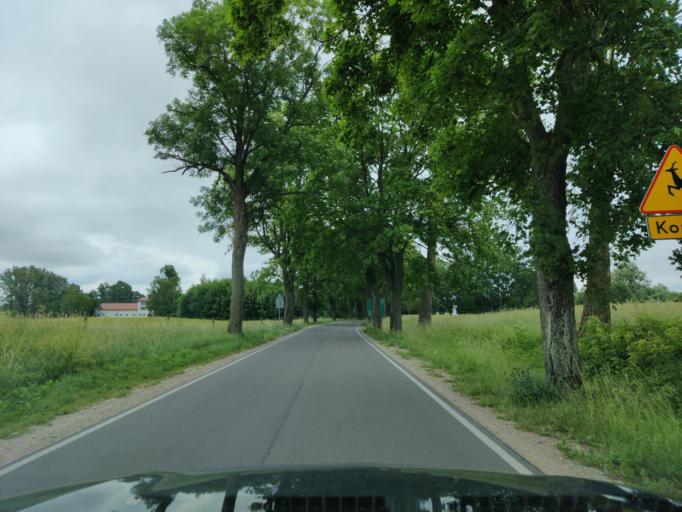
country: PL
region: Warmian-Masurian Voivodeship
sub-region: Powiat mragowski
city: Mikolajki
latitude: 53.8546
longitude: 21.6133
